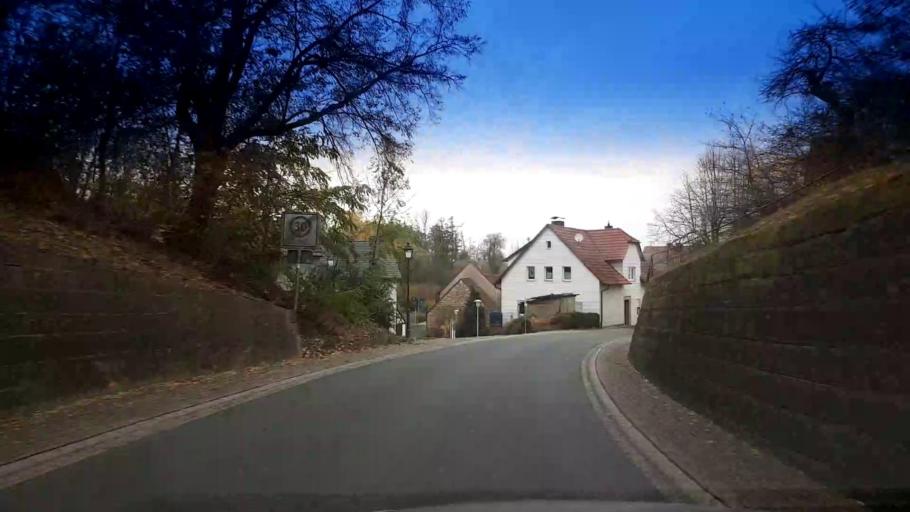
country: DE
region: Bavaria
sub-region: Upper Franconia
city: Rattelsdorf
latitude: 50.0166
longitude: 10.8862
